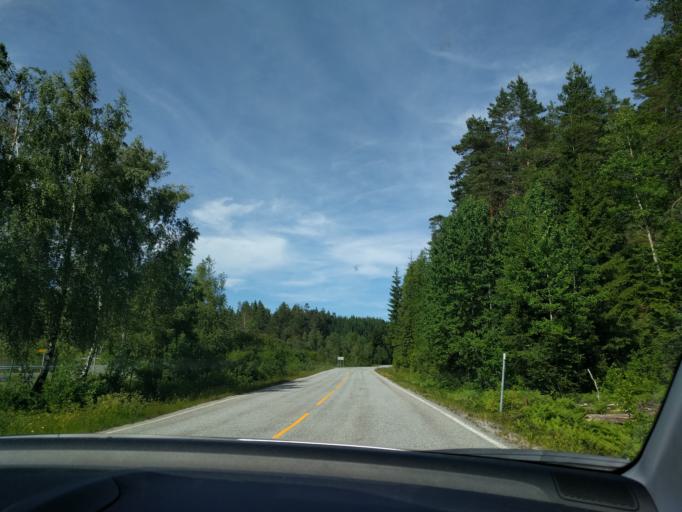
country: NO
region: Aust-Agder
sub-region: Gjerstad
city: Gjerstad
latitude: 58.8601
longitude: 9.1419
